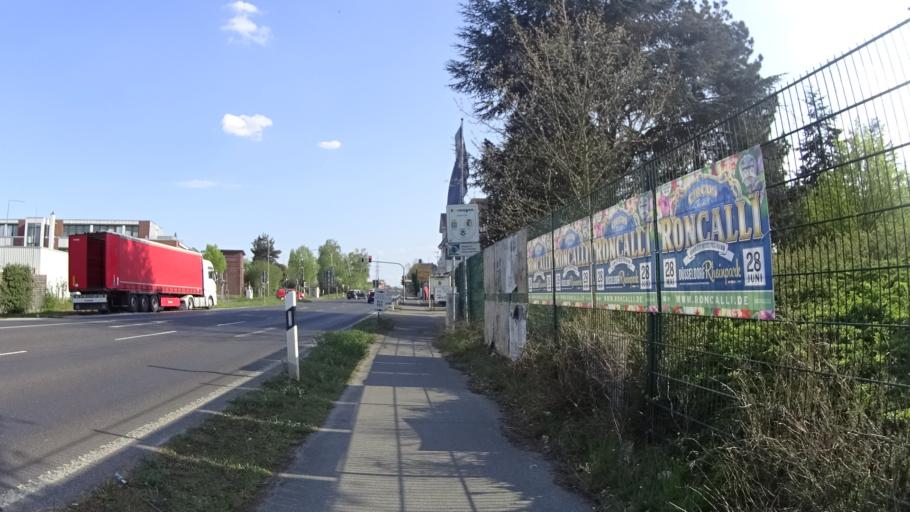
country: DE
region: North Rhine-Westphalia
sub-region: Regierungsbezirk Dusseldorf
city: Dormagen
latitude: 51.1365
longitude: 6.8013
